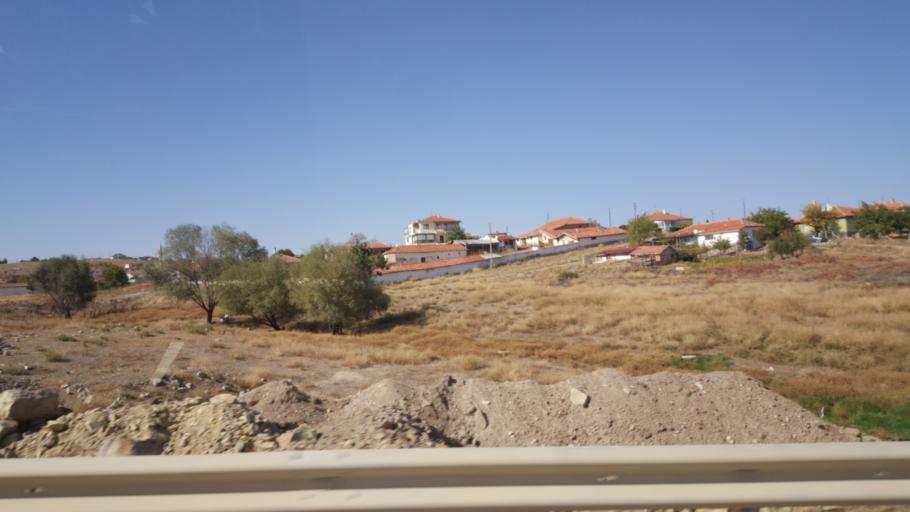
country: TR
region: Ankara
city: Ikizce
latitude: 39.6625
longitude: 32.7377
